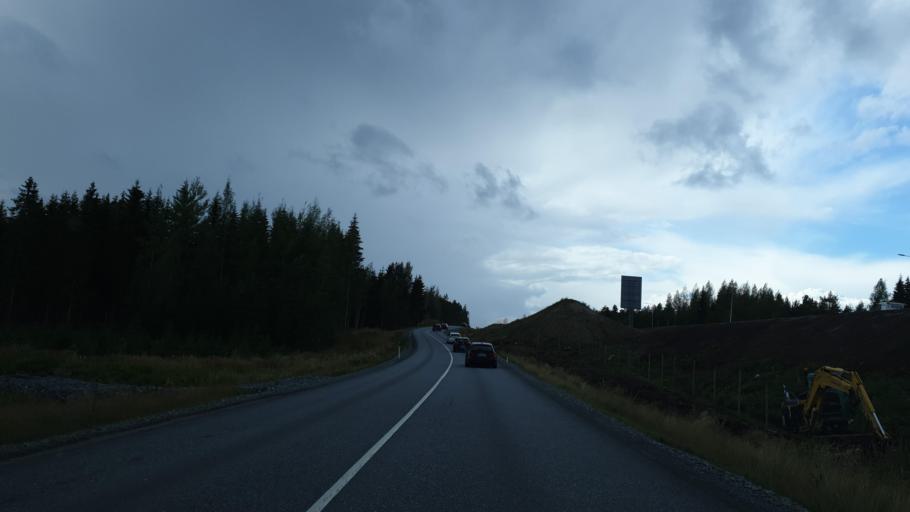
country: FI
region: Southern Savonia
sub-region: Pieksaemaeki
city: Juva
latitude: 61.8561
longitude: 27.7099
